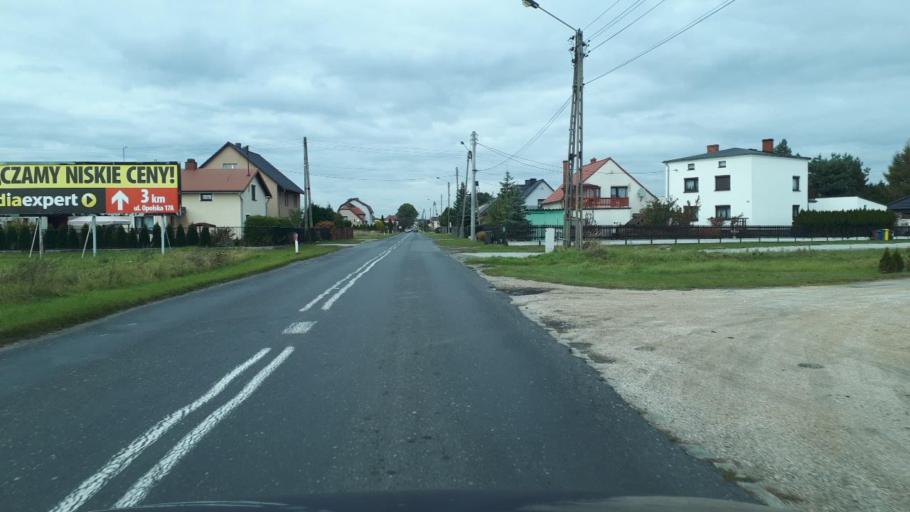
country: PL
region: Opole Voivodeship
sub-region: Powiat strzelecki
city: Zawadzkie
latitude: 50.5900
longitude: 18.5016
